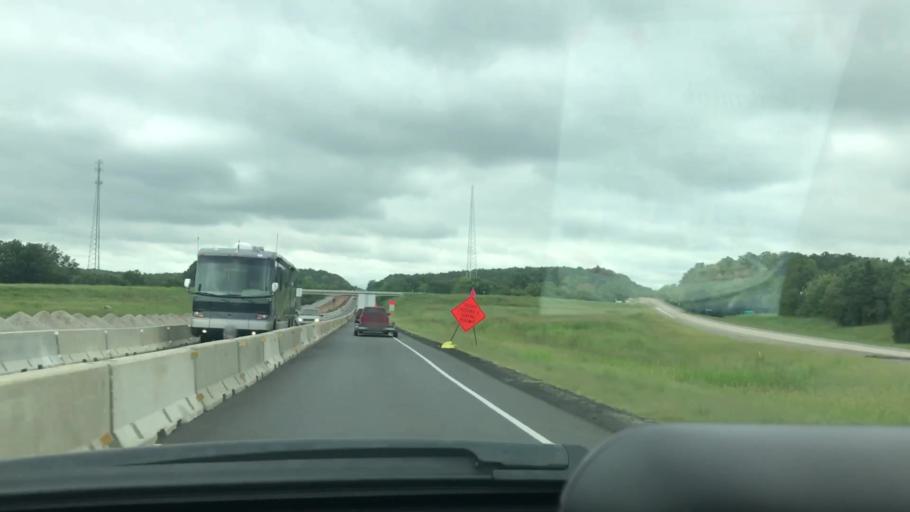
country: US
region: Oklahoma
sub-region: McIntosh County
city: Eufaula
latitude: 35.2602
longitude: -95.5883
